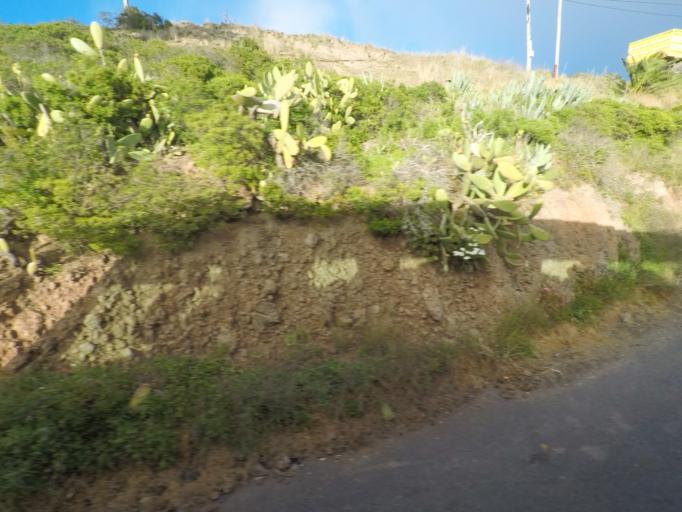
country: ES
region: Canary Islands
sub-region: Provincia de Santa Cruz de Tenerife
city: Alajero
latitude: 28.0986
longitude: -17.1828
